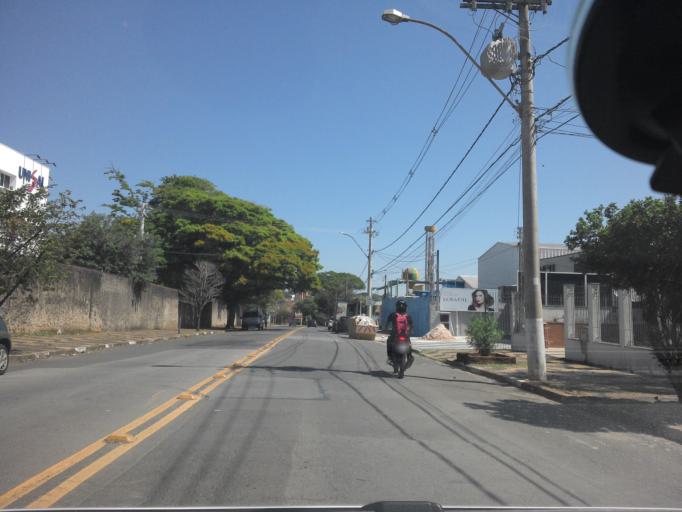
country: BR
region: Sao Paulo
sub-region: Campinas
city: Campinas
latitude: -22.8815
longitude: -47.0571
